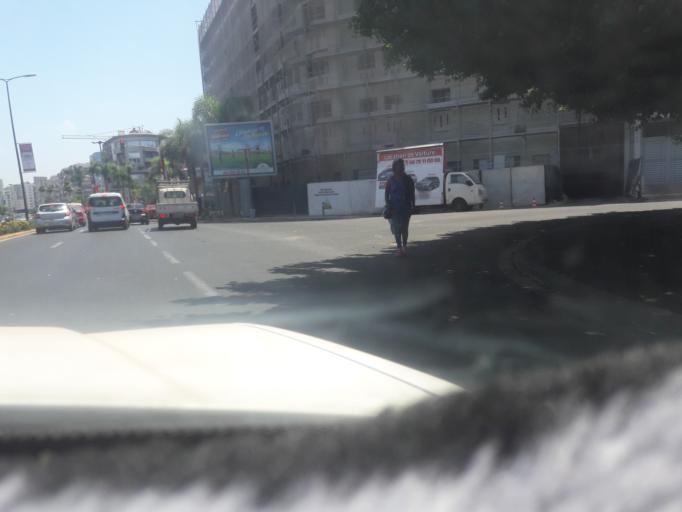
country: MA
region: Grand Casablanca
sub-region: Casablanca
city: Casablanca
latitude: 33.5877
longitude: -7.6452
